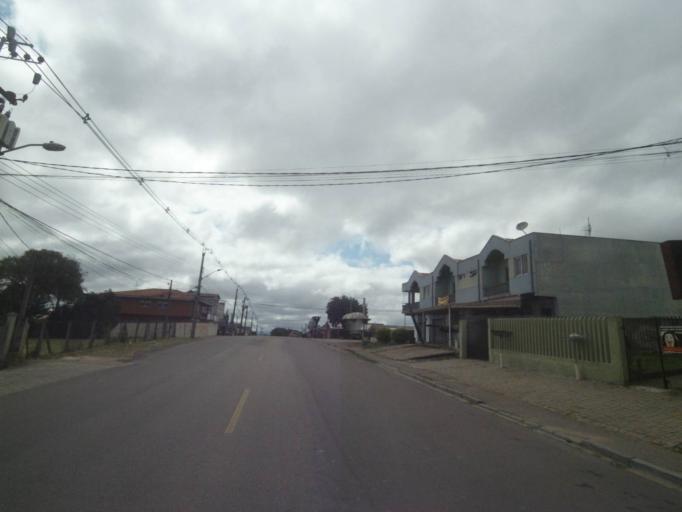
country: BR
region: Parana
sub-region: Sao Jose Dos Pinhais
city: Sao Jose dos Pinhais
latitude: -25.5448
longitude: -49.2863
